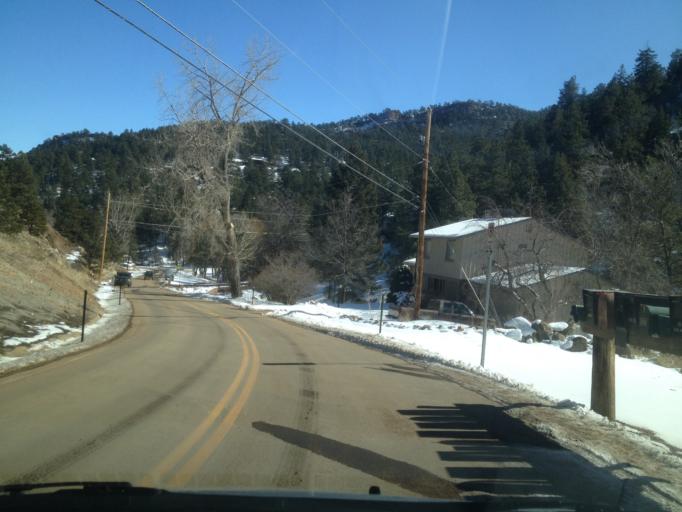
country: US
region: Colorado
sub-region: Boulder County
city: Boulder
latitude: 40.0610
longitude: -105.3181
